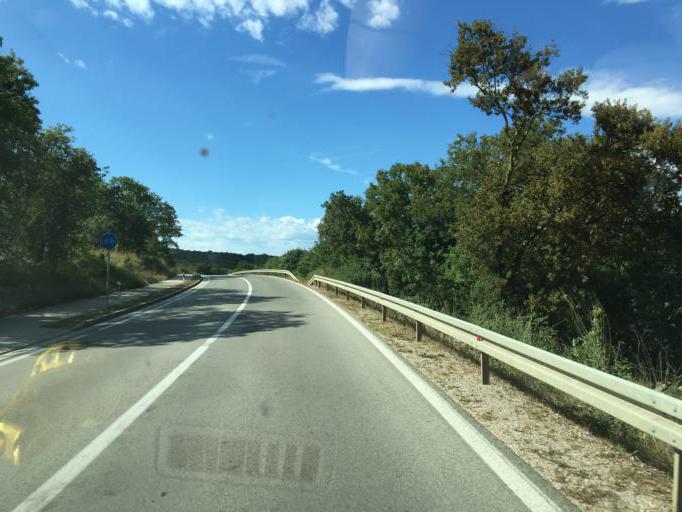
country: HR
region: Primorsko-Goranska
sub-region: Grad Krk
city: Krk
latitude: 45.0739
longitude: 14.5499
